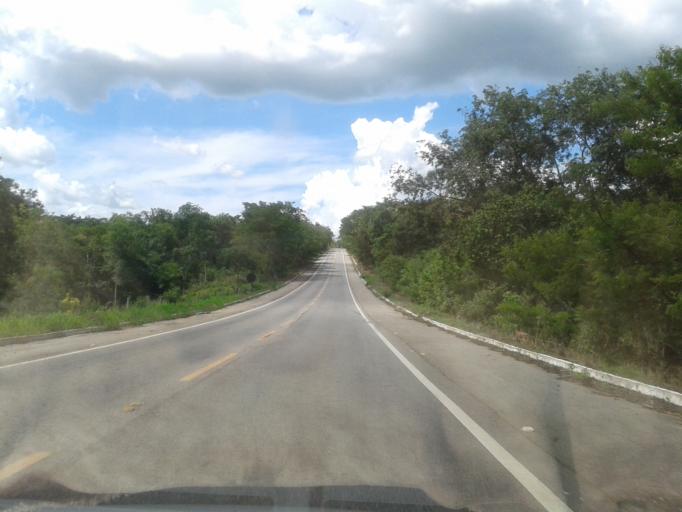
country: BR
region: Goias
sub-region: Goias
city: Goias
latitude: -15.8184
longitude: -50.1192
